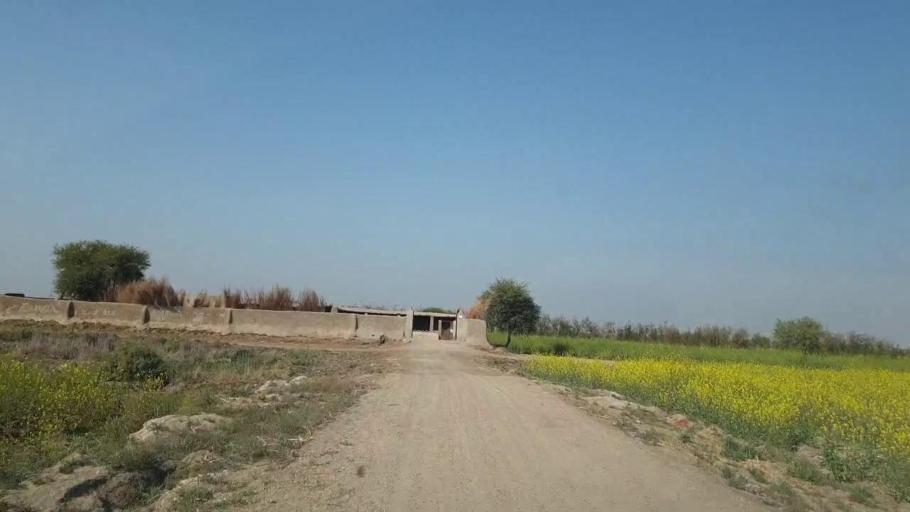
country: PK
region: Sindh
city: Mirpur Khas
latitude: 25.7384
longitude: 69.1564
